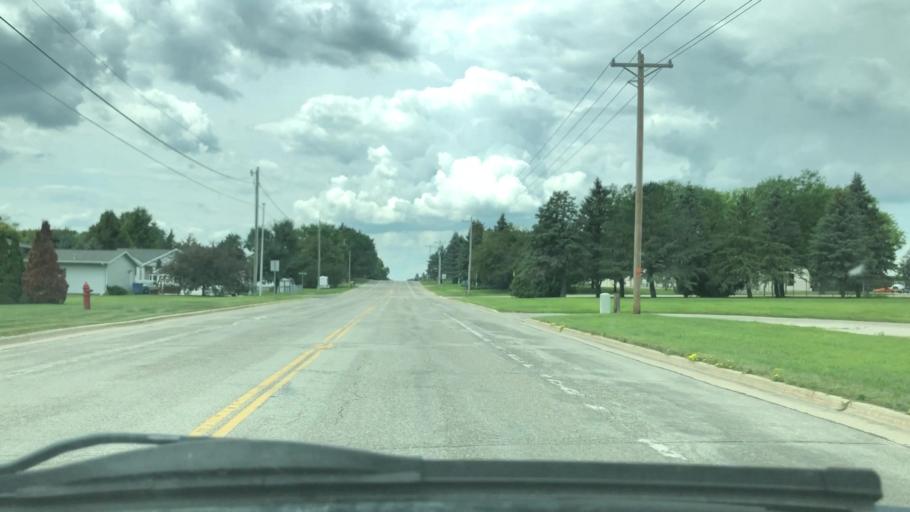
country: US
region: Minnesota
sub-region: Olmsted County
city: Stewartville
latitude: 43.8628
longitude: -92.4906
